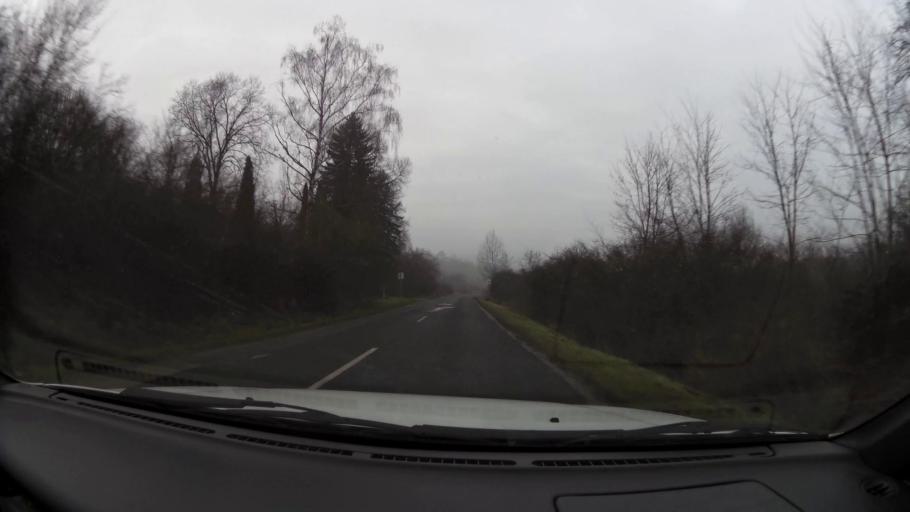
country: HU
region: Borsod-Abauj-Zemplen
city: Rudabanya
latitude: 48.3510
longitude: 20.6386
